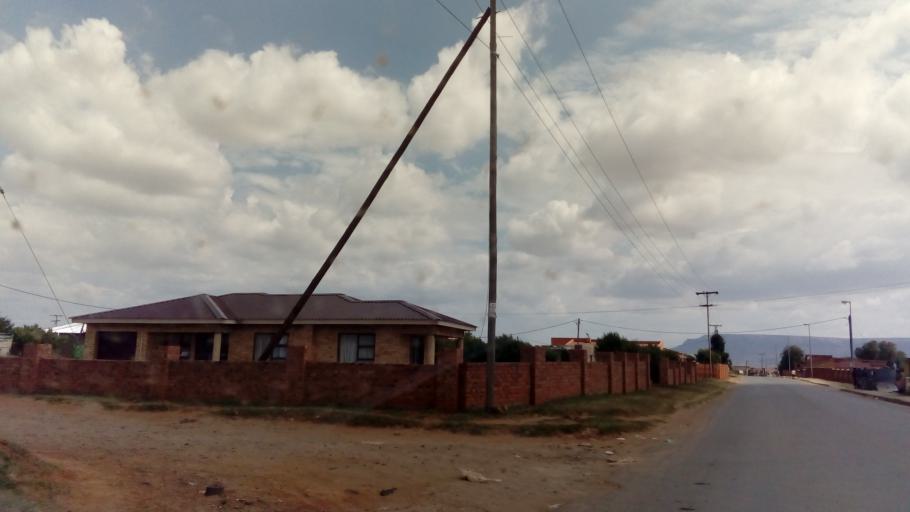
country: LS
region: Maseru
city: Maseru
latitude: -29.3844
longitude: 27.5288
